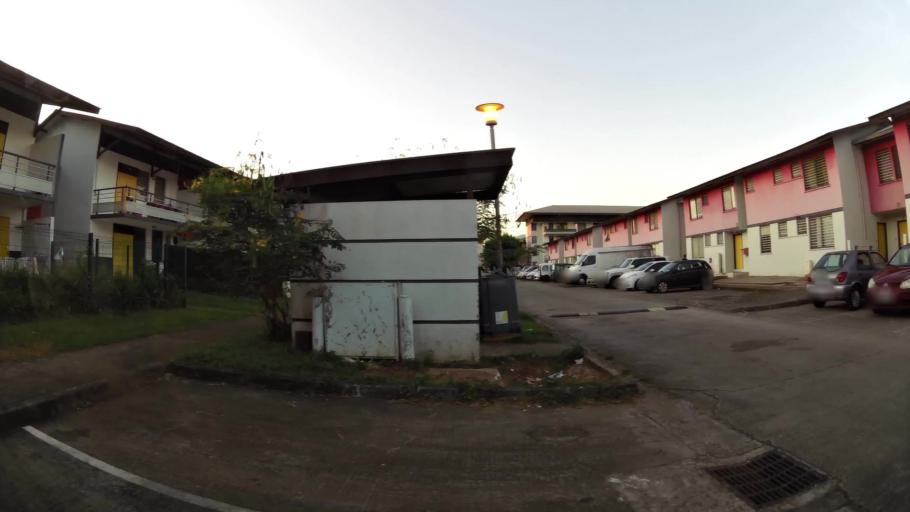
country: GF
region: Guyane
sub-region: Guyane
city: Cayenne
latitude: 4.9232
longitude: -52.3143
